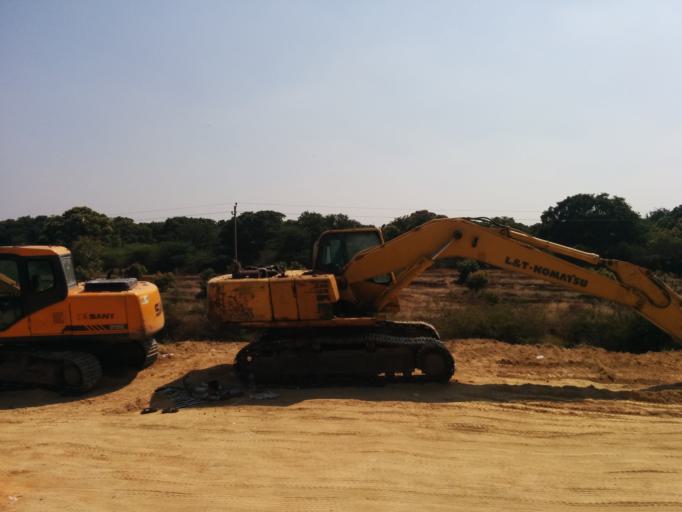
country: IN
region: Karnataka
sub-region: Gadag
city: Gadag
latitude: 15.4364
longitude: 75.5390
